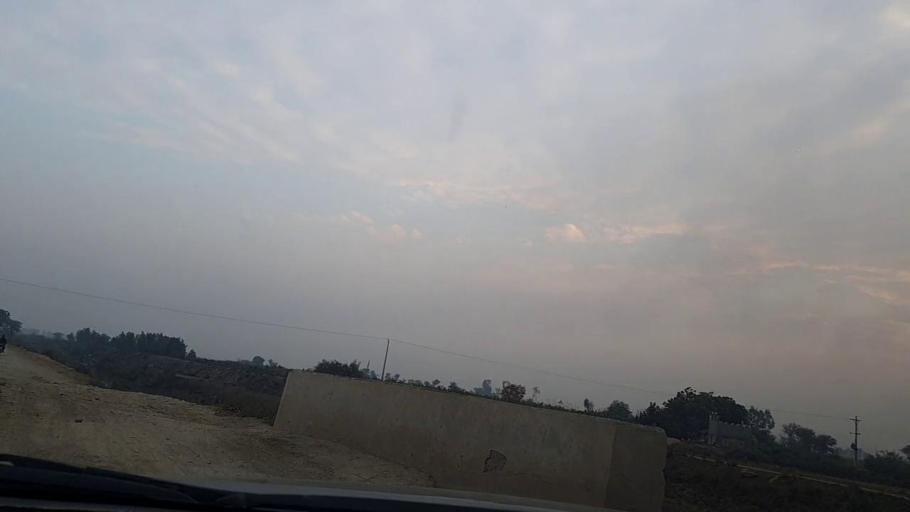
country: PK
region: Sindh
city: Sakrand
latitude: 26.2890
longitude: 68.2371
